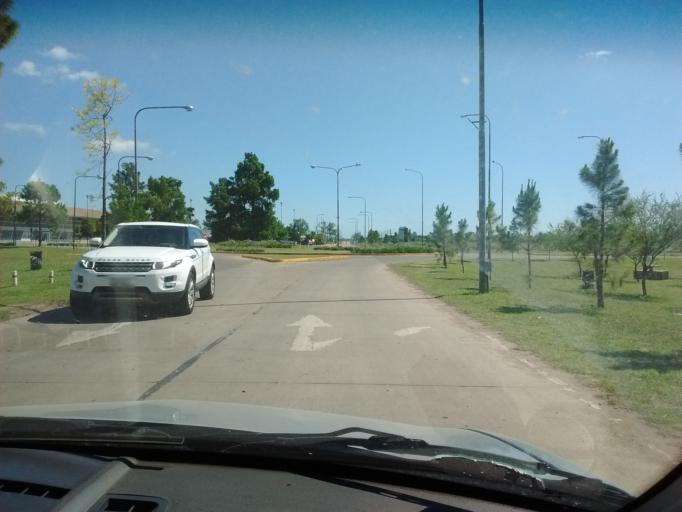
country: AR
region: Santa Fe
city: Funes
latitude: -32.9186
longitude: -60.7800
